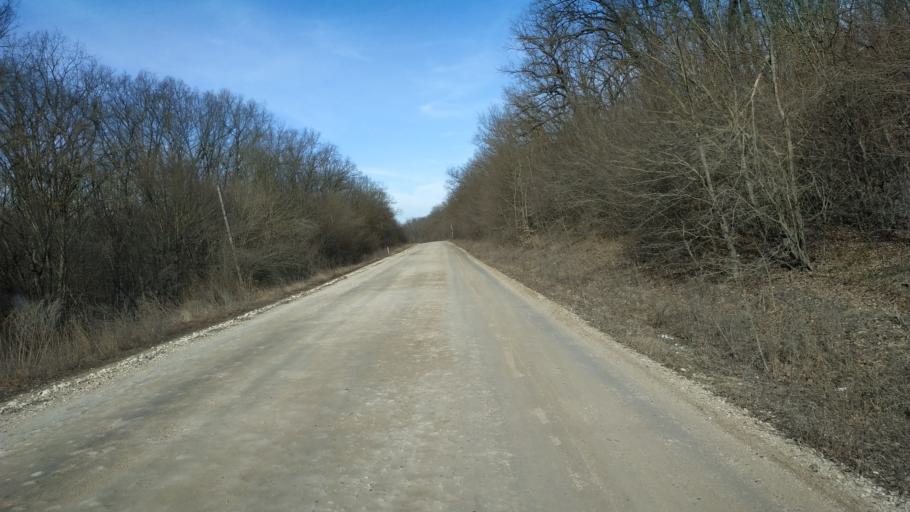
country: MD
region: Straseni
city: Straseni
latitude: 47.0363
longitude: 28.6144
